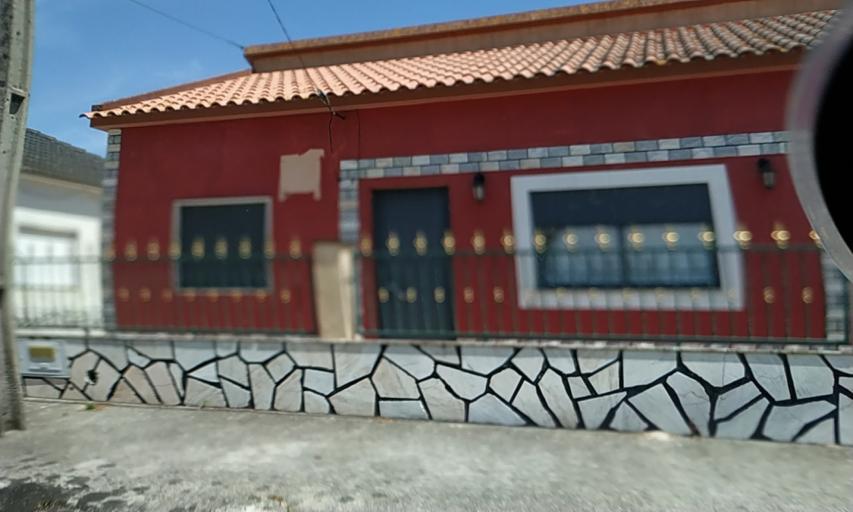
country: PT
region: Santarem
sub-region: Benavente
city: Poceirao
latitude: 38.6802
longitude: -8.7327
